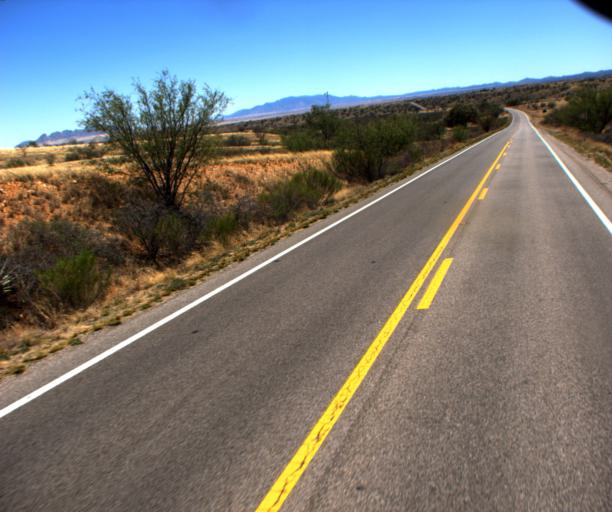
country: US
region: Arizona
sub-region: Pima County
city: Corona de Tucson
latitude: 31.7939
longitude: -110.7009
